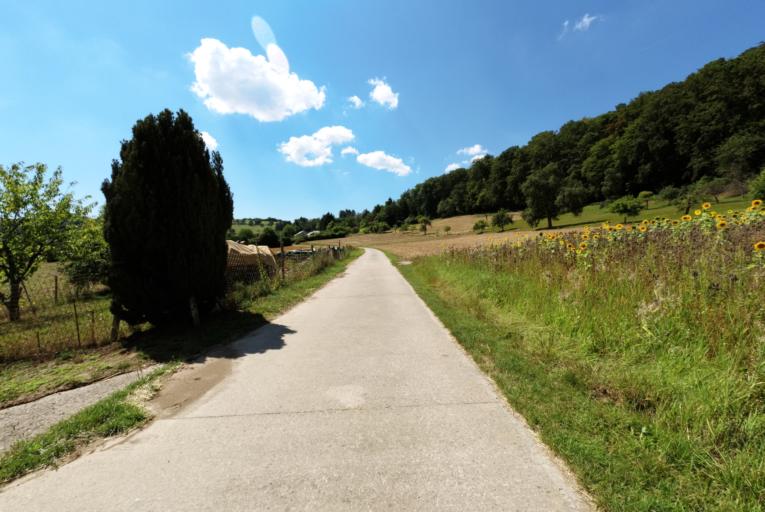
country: DE
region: Baden-Wuerttemberg
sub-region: Karlsruhe Region
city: Neunkirchen
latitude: 49.3871
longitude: 9.0370
